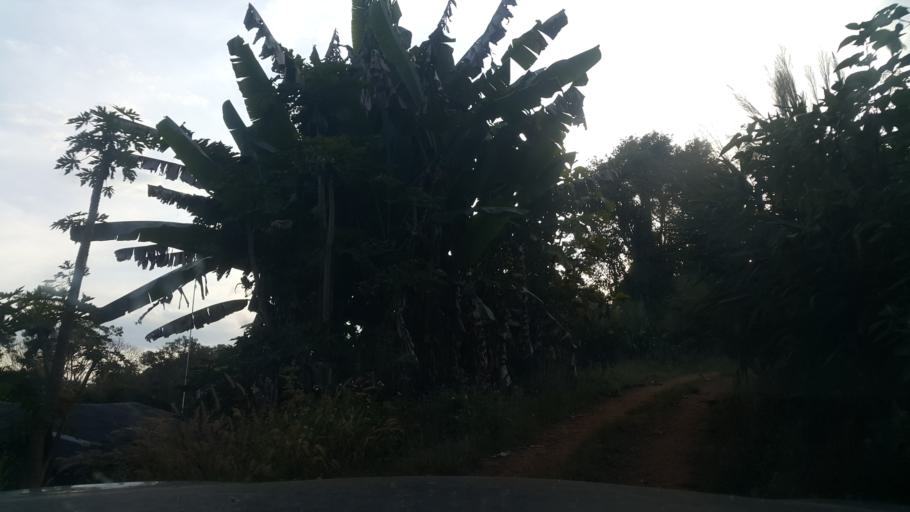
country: TH
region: Chiang Mai
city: Samoeng
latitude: 19.0083
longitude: 98.6471
